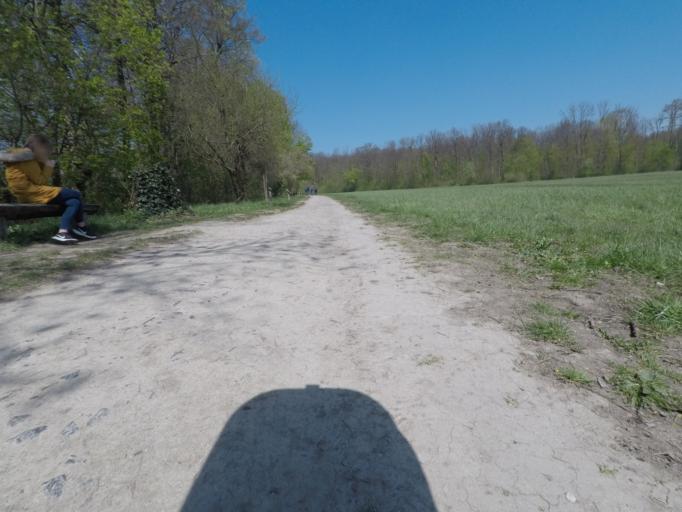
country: AT
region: Lower Austria
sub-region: Politischer Bezirk Modling
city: Perchtoldsdorf
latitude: 48.1685
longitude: 16.2538
